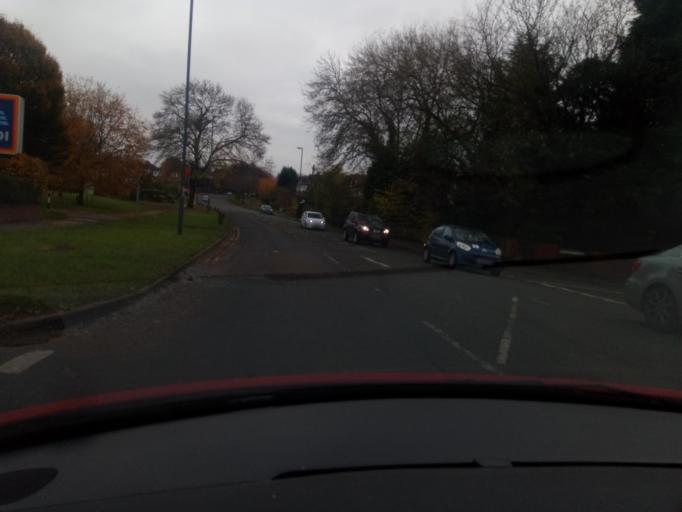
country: GB
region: England
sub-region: Derby
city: Derby
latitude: 52.9235
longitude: -1.4366
